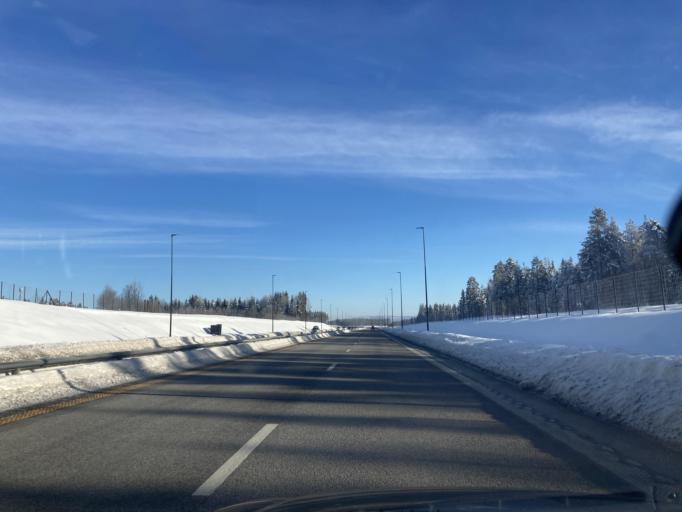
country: NO
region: Hedmark
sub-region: Loten
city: Loten
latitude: 60.8625
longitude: 11.4202
